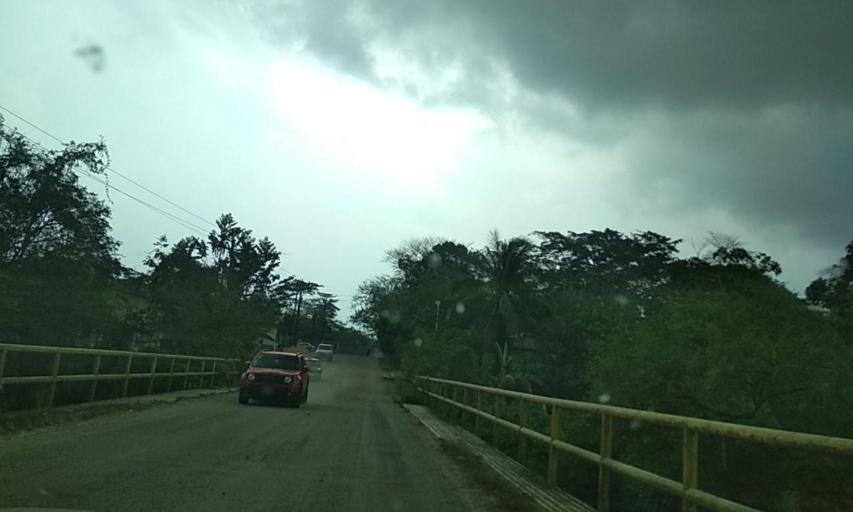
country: MX
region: Tabasco
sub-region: Huimanguillo
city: Francisco Rueda
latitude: 17.5638
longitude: -94.1151
